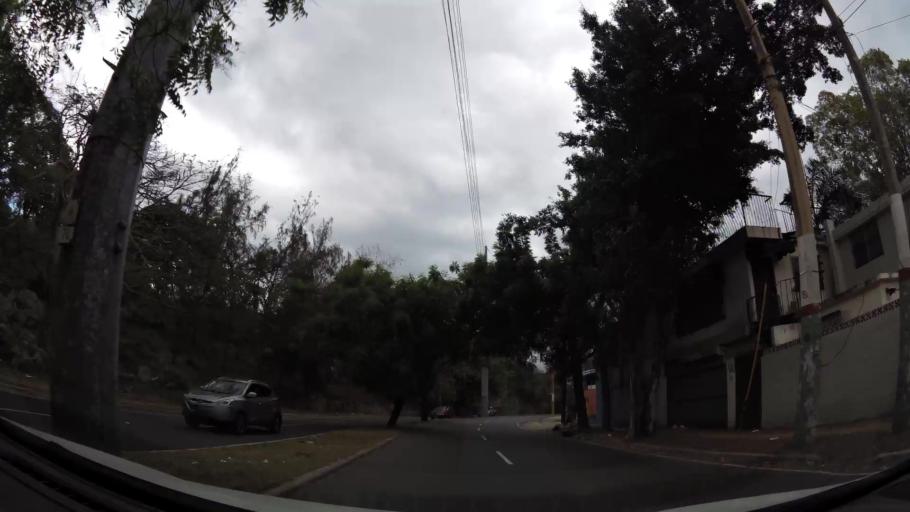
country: DO
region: Nacional
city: Bella Vista
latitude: 18.4473
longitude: -69.9419
